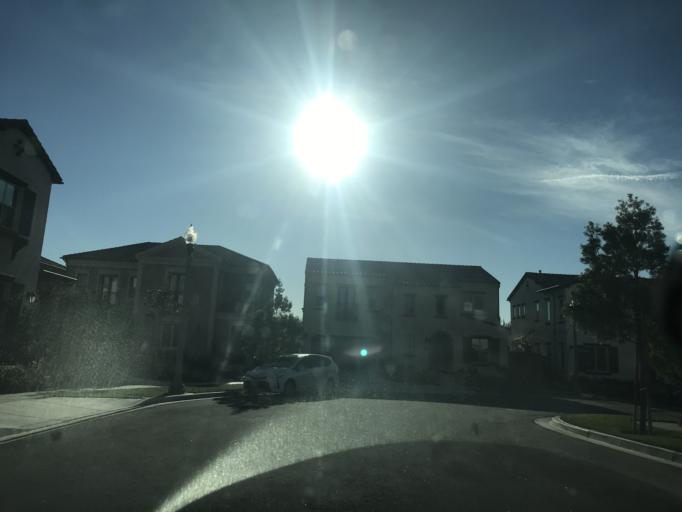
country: US
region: California
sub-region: Orange County
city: North Tustin
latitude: 33.7112
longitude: -117.7396
